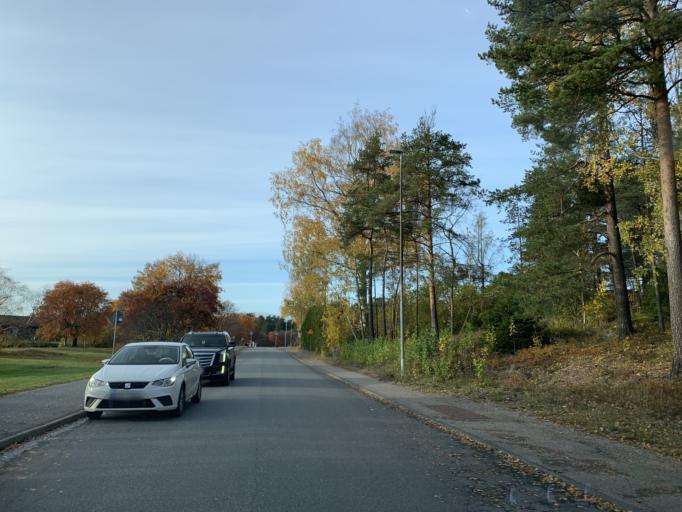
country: SE
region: Stockholm
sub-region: Haninge Kommun
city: Haninge
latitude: 59.1752
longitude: 18.1853
